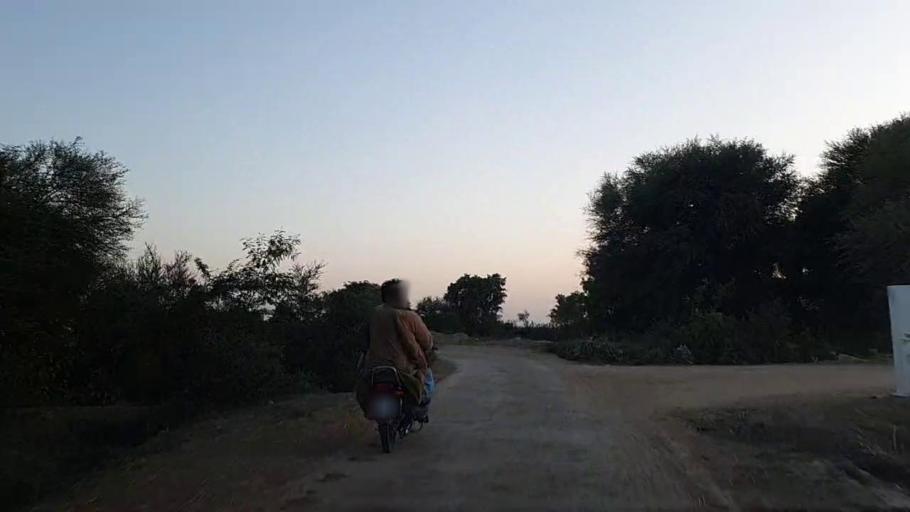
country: PK
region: Sindh
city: Mirpur Batoro
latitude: 24.6170
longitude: 68.1836
